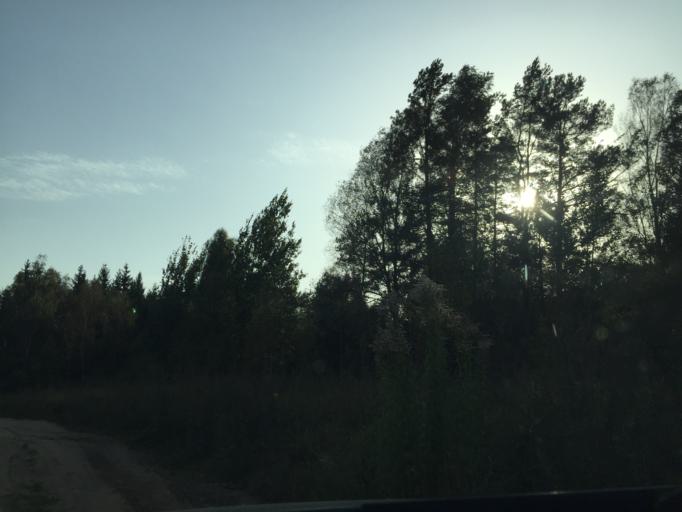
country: LV
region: Garkalne
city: Garkalne
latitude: 56.9719
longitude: 24.4171
